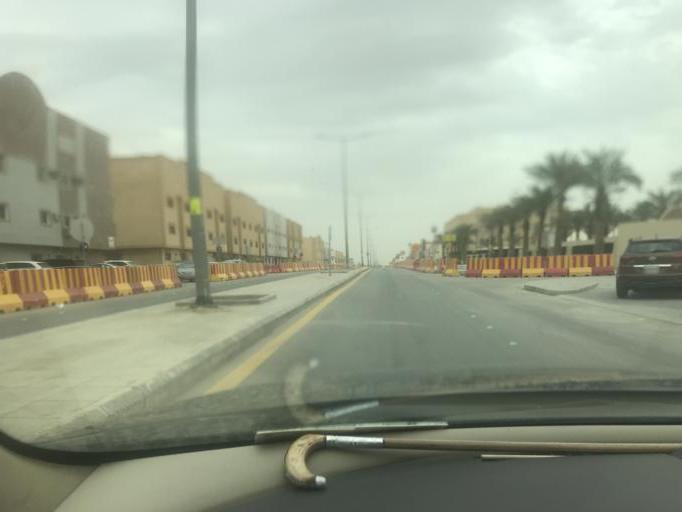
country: SA
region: Ar Riyad
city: Riyadh
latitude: 24.7943
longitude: 46.7093
